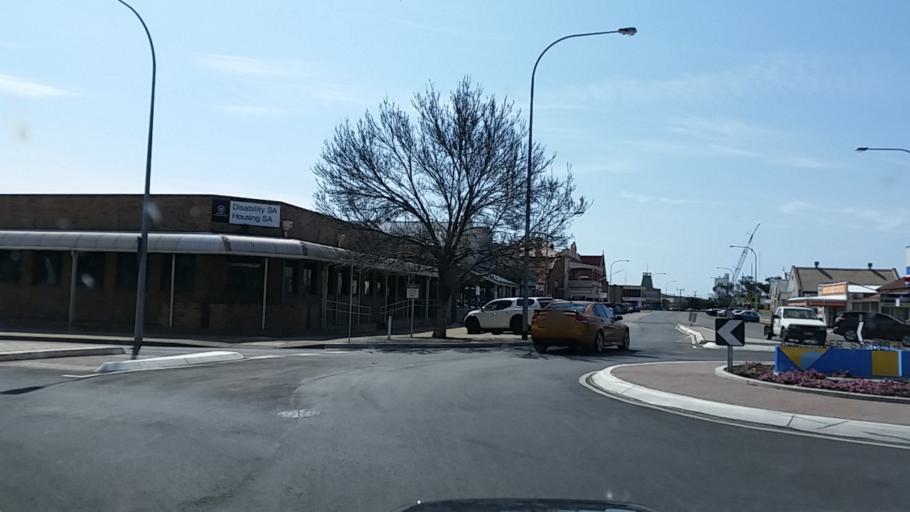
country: AU
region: South Australia
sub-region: Port Pirie City and Dists
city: Port Pirie
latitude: -33.1775
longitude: 138.0086
